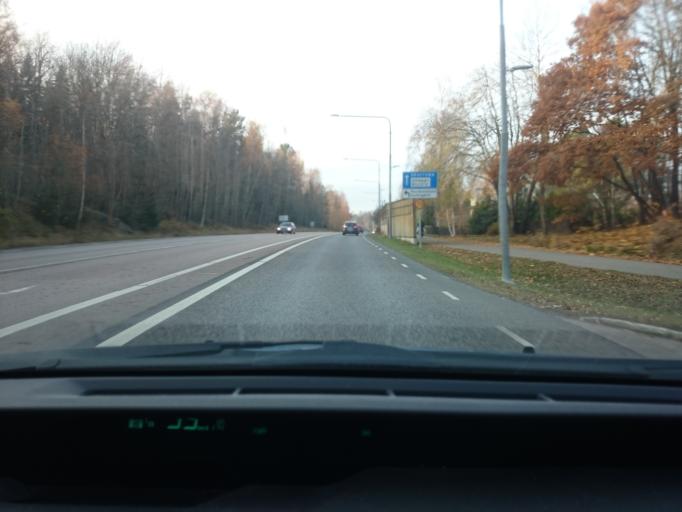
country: SE
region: Vaestmanland
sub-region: Vasteras
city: Vasteras
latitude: 59.6379
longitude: 16.5193
